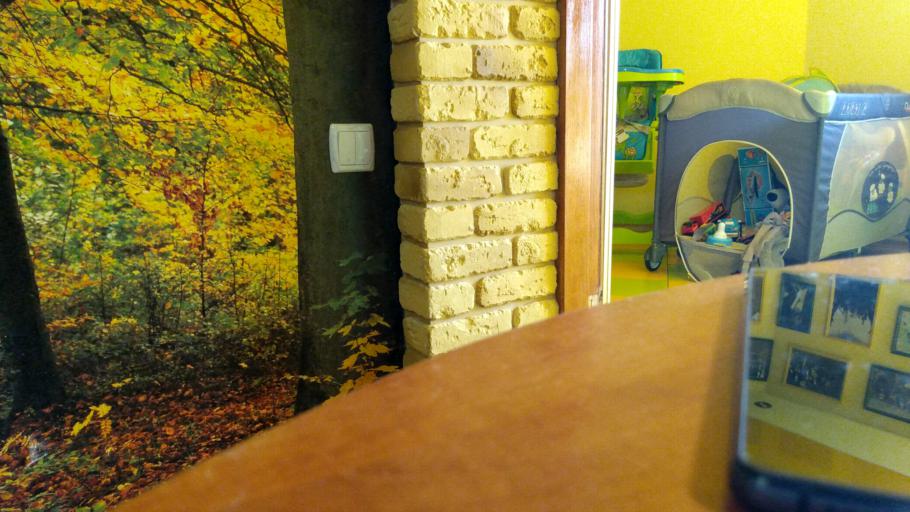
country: RU
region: Tverskaya
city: Kalashnikovo
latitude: 57.2739
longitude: 35.3853
